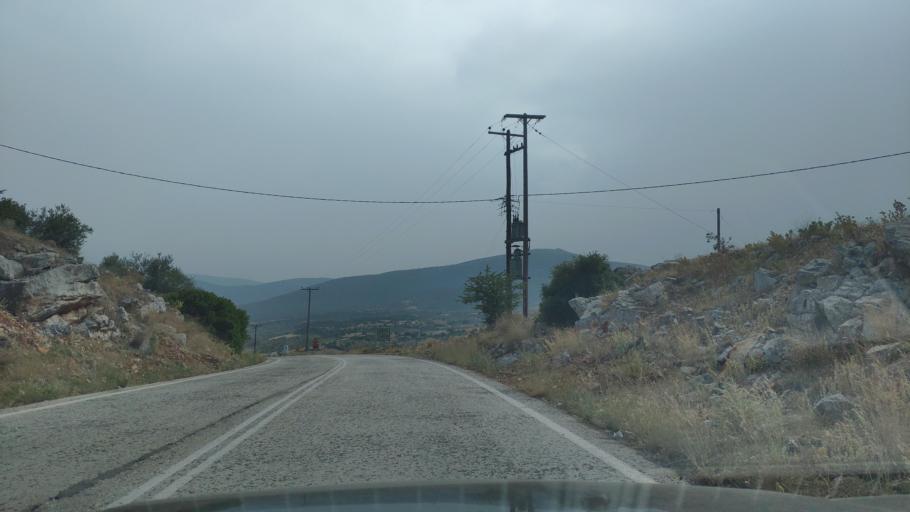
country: GR
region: Peloponnese
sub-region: Nomos Argolidos
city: Palaia Epidavros
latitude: 37.6010
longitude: 23.1575
